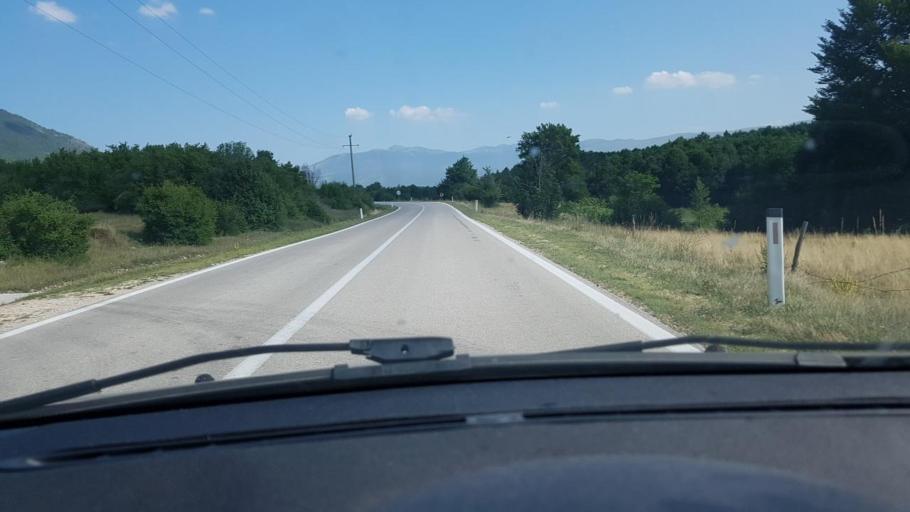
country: BA
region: Federation of Bosnia and Herzegovina
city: Glamoc
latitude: 44.0115
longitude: 16.6034
